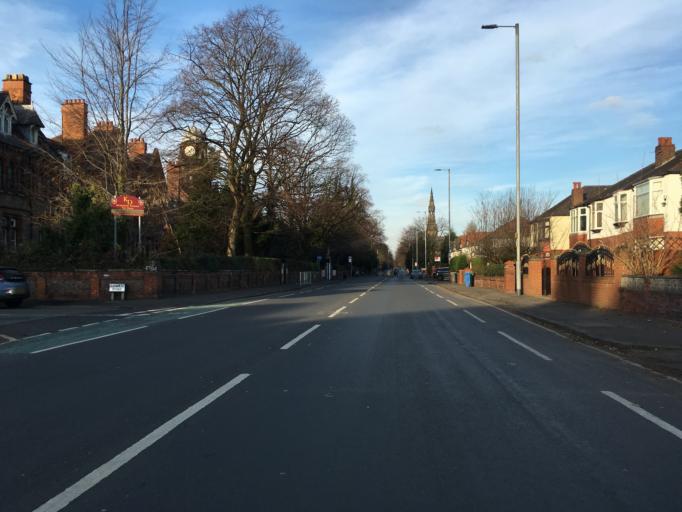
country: GB
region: England
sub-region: Manchester
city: Chorlton cum Hardy
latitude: 53.4447
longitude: -2.2517
